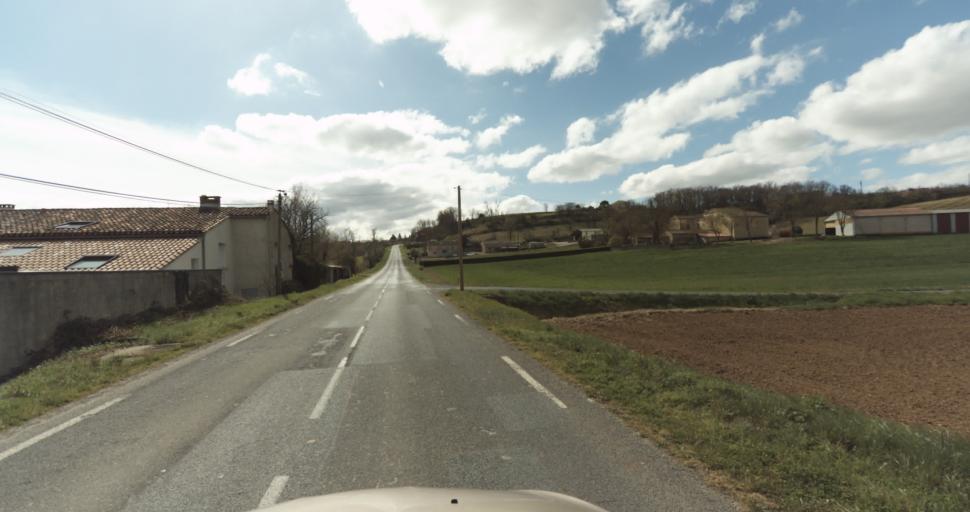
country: FR
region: Midi-Pyrenees
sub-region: Departement du Tarn
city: Puygouzon
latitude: 43.8866
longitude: 2.1541
